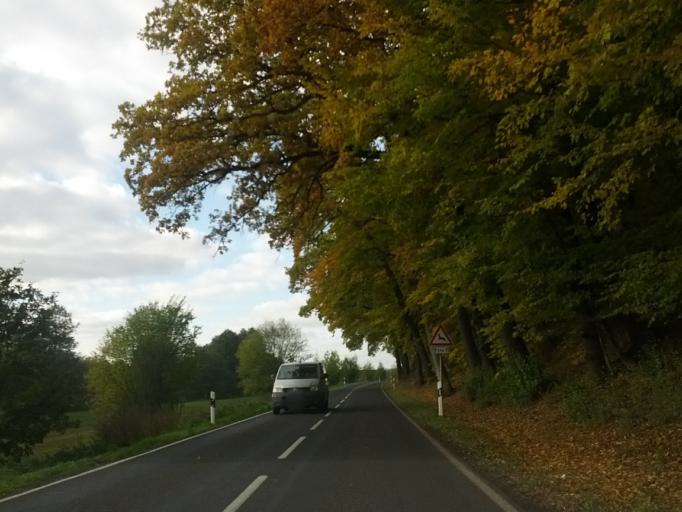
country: DE
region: Thuringia
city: Marksuhl
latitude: 50.9215
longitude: 10.1770
